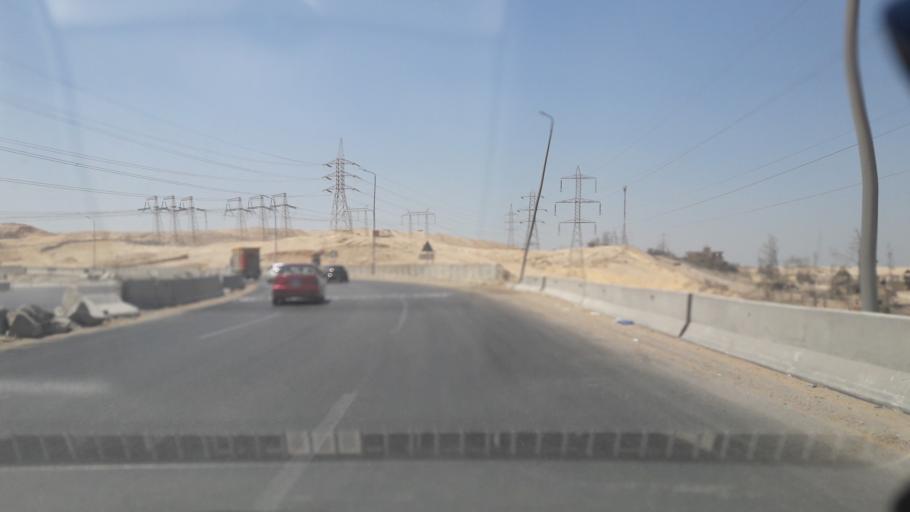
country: EG
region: Al Jizah
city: Awsim
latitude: 30.0226
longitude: 31.0810
